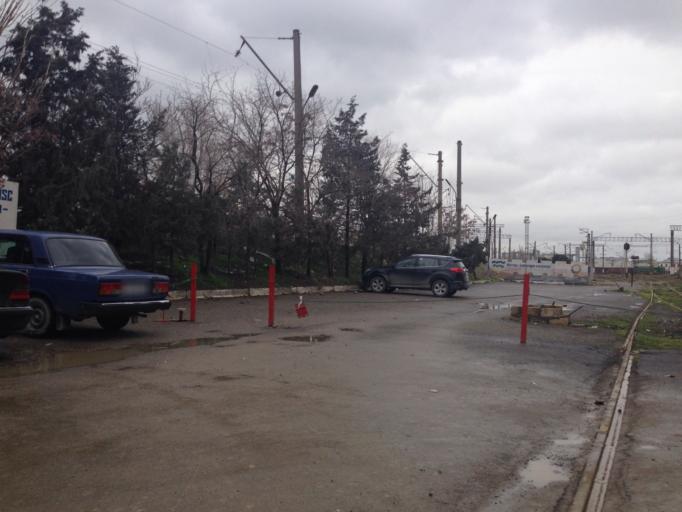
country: AZ
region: Baki
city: Baku
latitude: 40.4125
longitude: 49.8732
